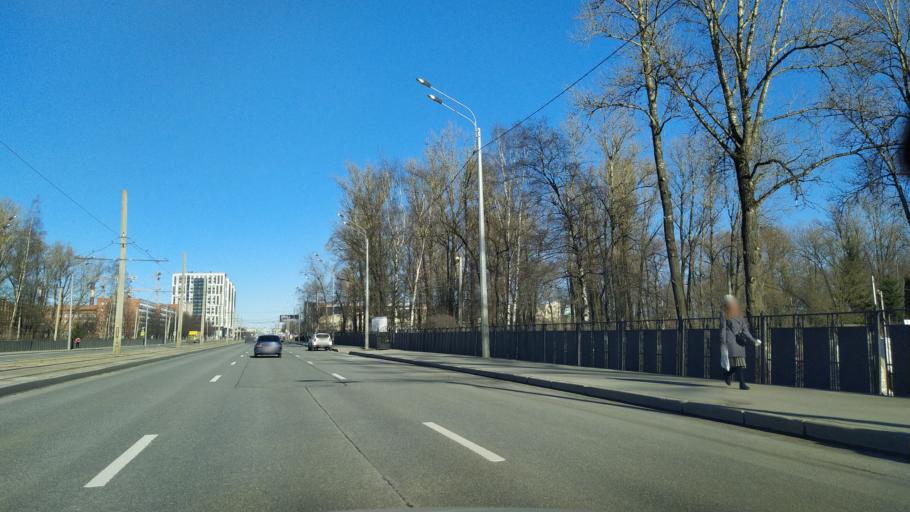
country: RU
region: St.-Petersburg
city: Kupchino
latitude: 59.8808
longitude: 30.3598
